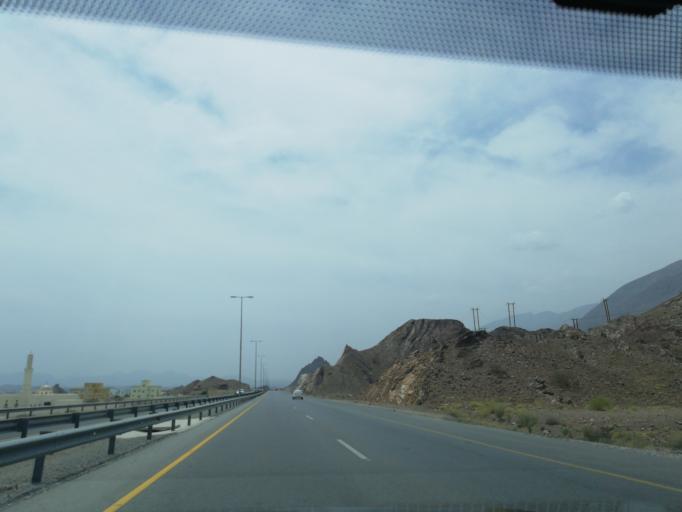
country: OM
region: Muhafazat ad Dakhiliyah
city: Sufalat Sama'il
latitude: 23.2981
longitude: 57.9406
